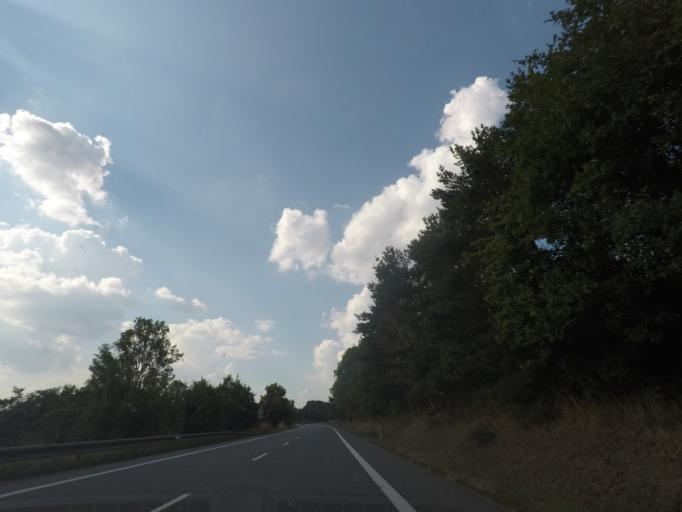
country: CZ
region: Kralovehradecky
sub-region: Okres Nachod
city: Jaromer
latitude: 50.3987
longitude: 15.8974
